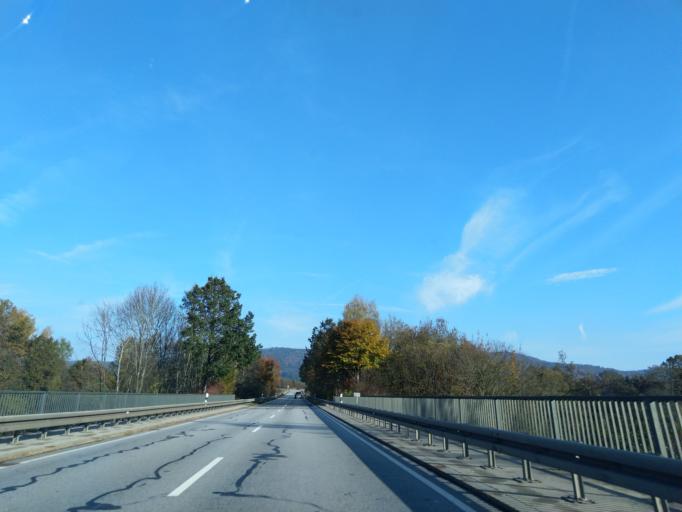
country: DE
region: Bavaria
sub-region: Lower Bavaria
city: Lalling
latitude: 48.8316
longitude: 13.1479
